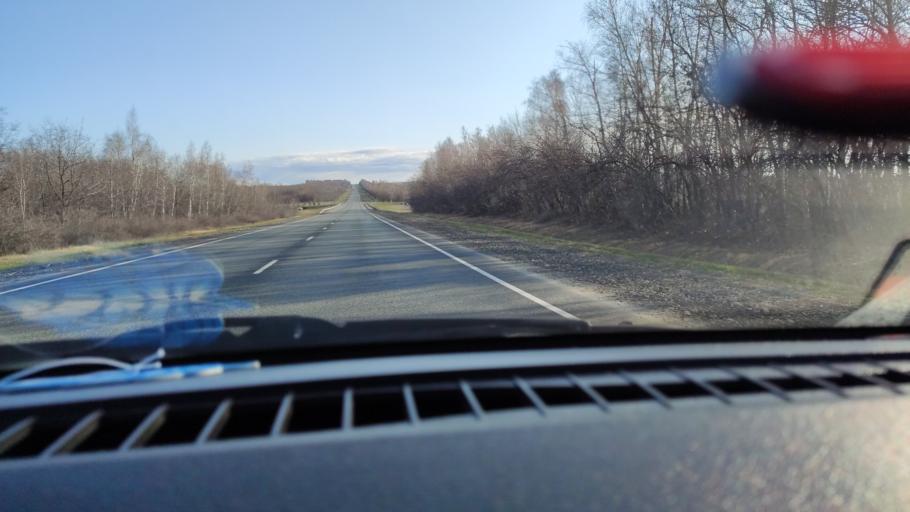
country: RU
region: Saratov
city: Khvalynsk
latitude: 52.6076
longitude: 48.1541
